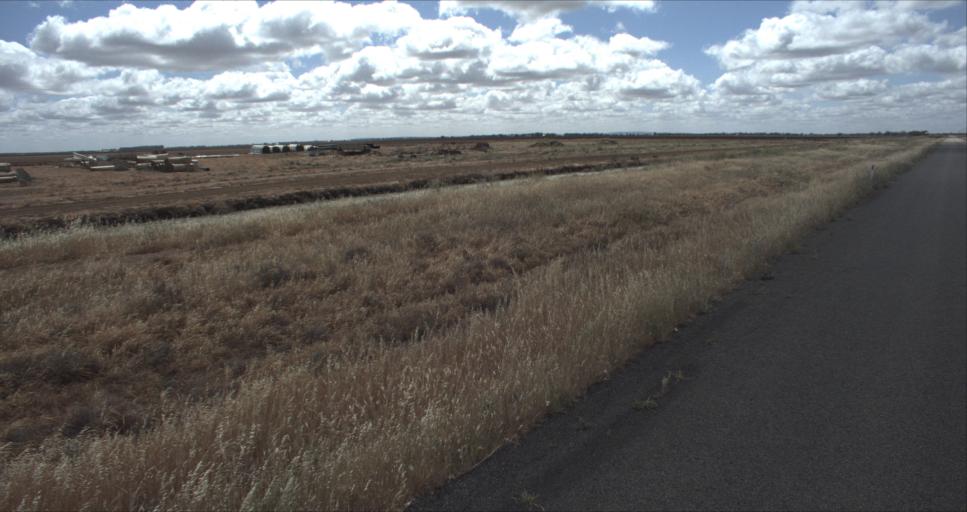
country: AU
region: New South Wales
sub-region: Murrumbidgee Shire
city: Darlington Point
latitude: -34.5779
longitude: 146.1926
